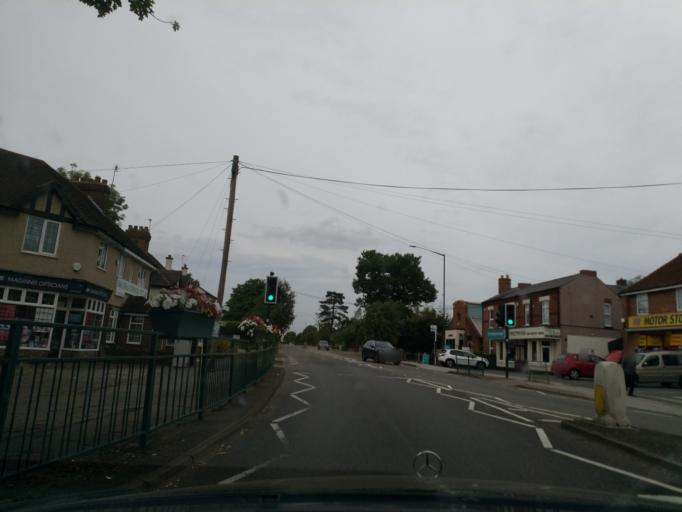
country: GB
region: England
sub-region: Solihull
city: Balsall Common
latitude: 52.3918
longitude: -1.6503
